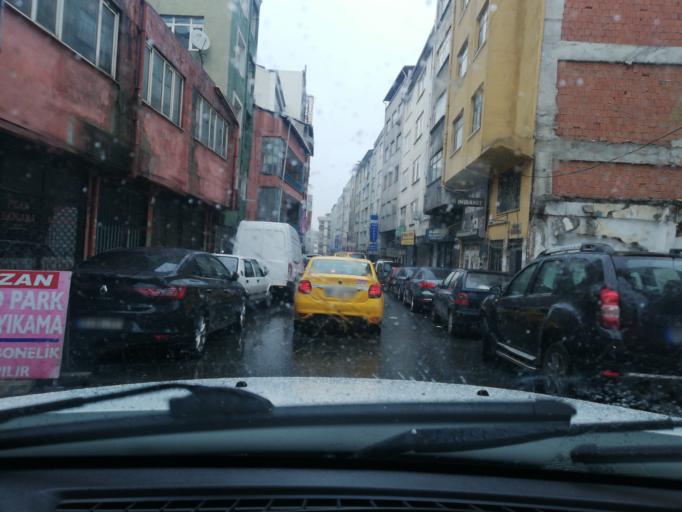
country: TR
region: Istanbul
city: Sisli
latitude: 41.0761
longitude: 28.9822
